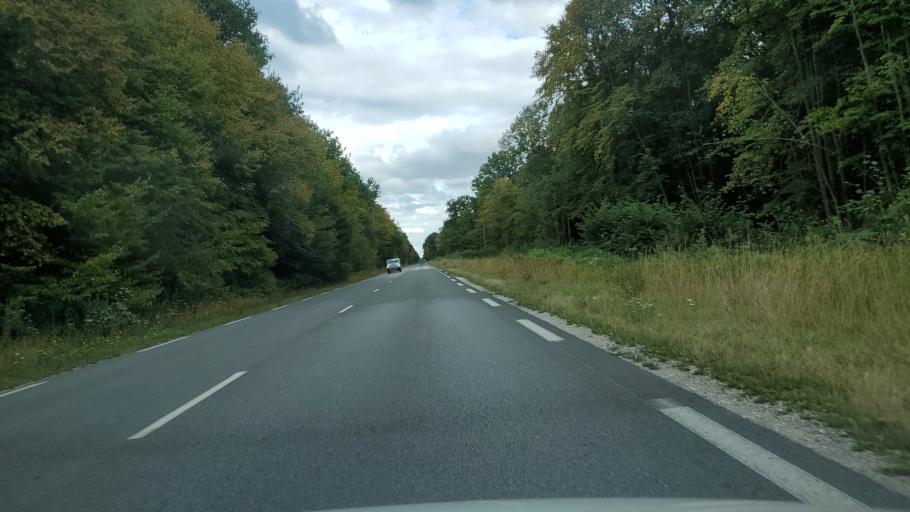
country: FR
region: Ile-de-France
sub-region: Departement de Seine-et-Marne
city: Mortcerf
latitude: 48.7606
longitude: 2.9286
